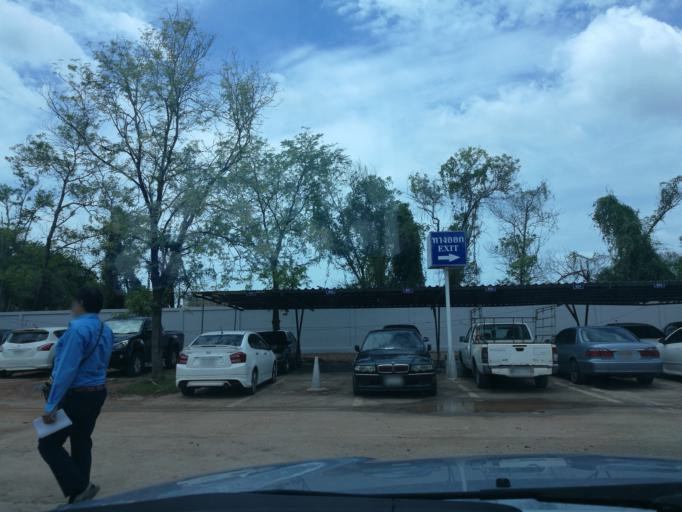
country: TH
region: Bangkok
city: Bang Khun Thian
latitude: 13.6211
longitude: 100.4393
